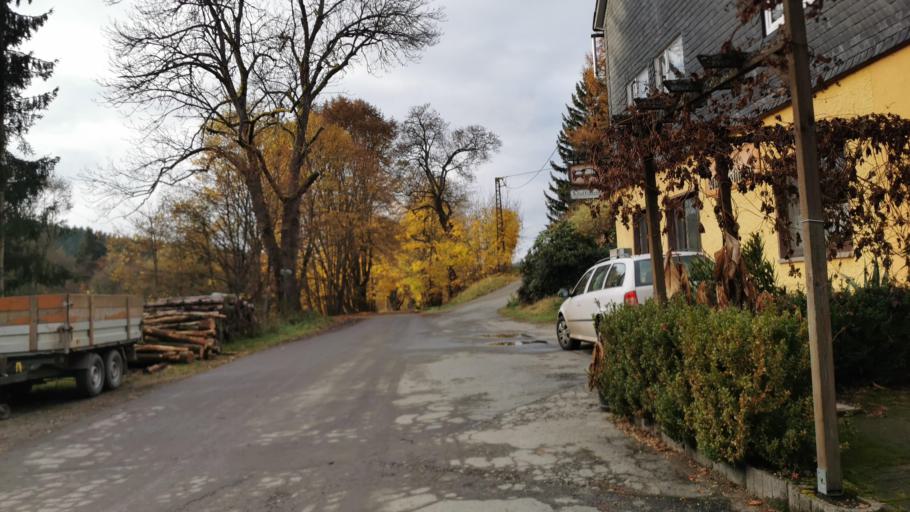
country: DE
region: Thuringia
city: Wurzbach
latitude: 50.4507
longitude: 11.5459
